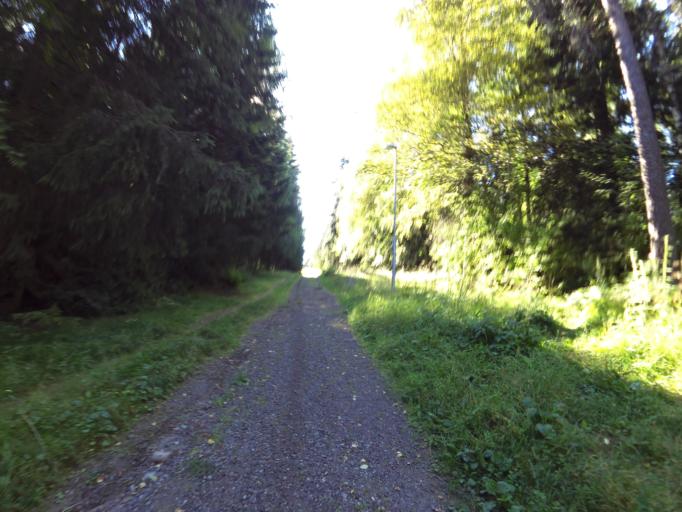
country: FI
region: Pirkanmaa
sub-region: Tampere
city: Pirkkala
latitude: 61.5088
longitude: 23.6234
